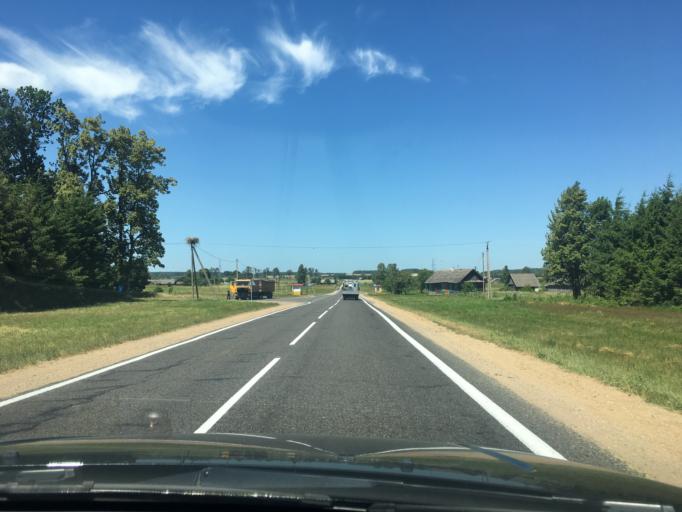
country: BY
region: Grodnenskaya
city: Hal'shany
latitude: 54.0974
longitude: 25.9177
